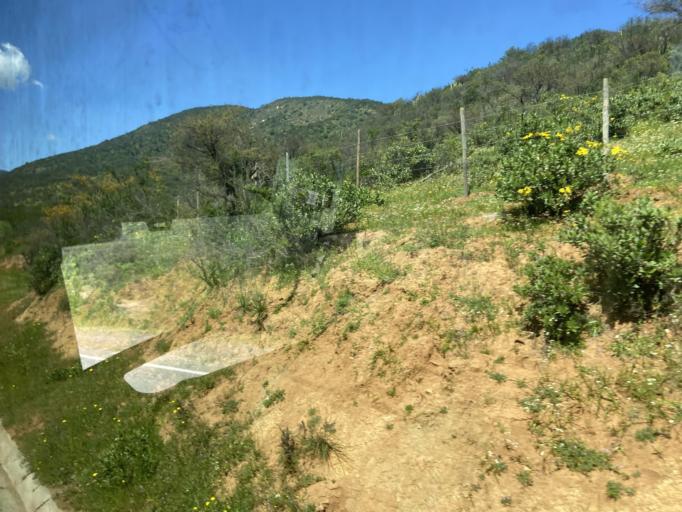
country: CL
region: Valparaiso
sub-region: Provincia de Marga Marga
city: Villa Alemana
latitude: -33.1904
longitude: -71.2879
